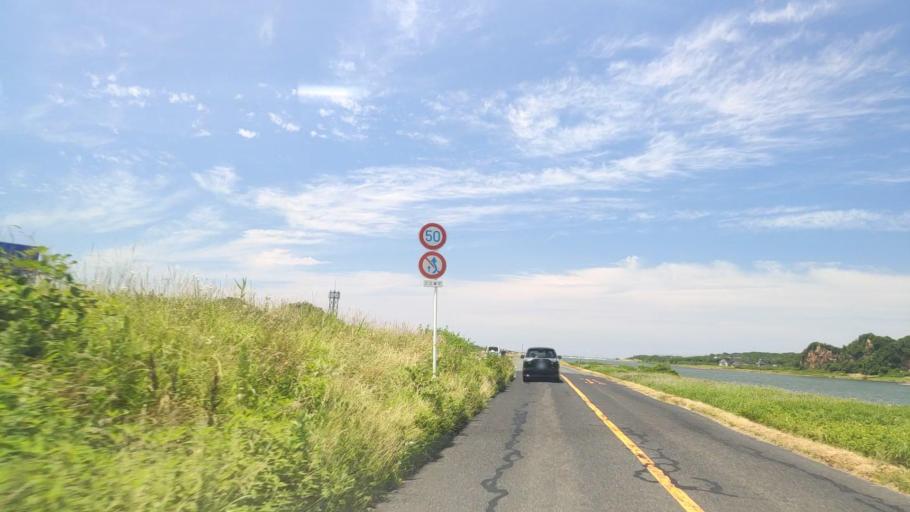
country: JP
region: Tottori
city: Tottori
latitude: 35.5240
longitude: 134.2056
